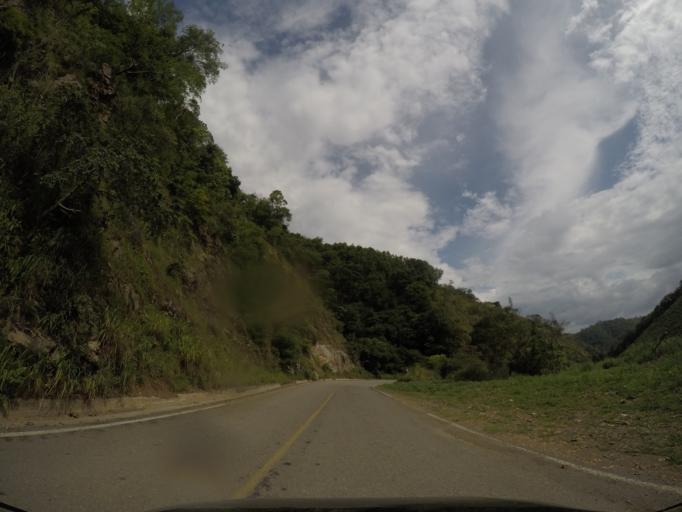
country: MX
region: Oaxaca
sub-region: San Jeronimo Coatlan
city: San Cristobal Honduras
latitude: 16.3849
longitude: -97.0758
